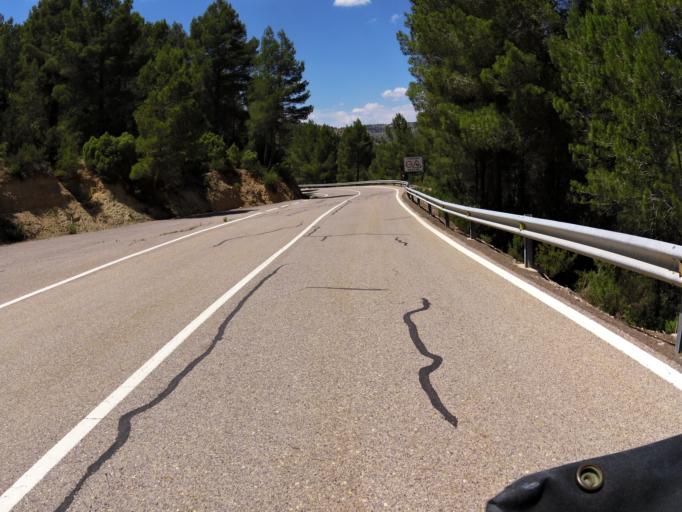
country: ES
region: Castille-La Mancha
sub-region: Provincia de Cuenca
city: Santa Cruz de Moya
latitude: 39.9812
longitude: -1.2740
